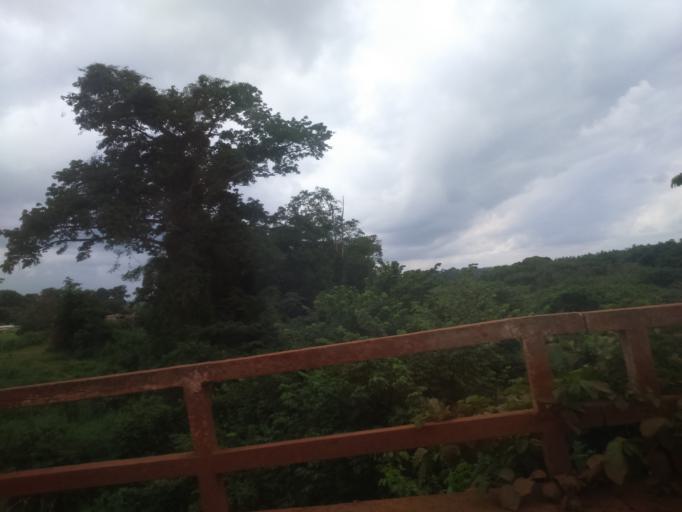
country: CI
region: Moyen-Comoe
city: Abengourou
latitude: 6.6383
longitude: -3.7133
